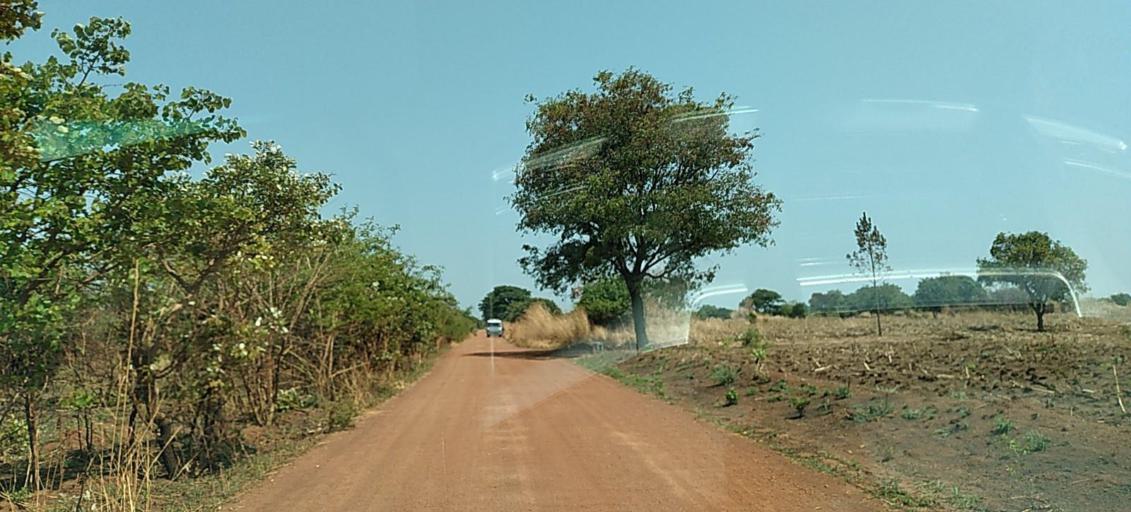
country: ZM
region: Copperbelt
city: Chingola
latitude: -12.5388
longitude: 27.7287
